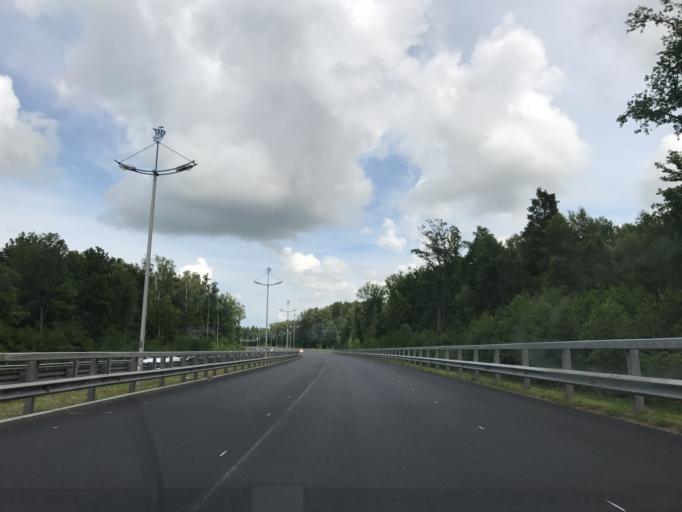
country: RU
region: Kaliningrad
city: Gur'yevsk
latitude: 54.8257
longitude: 20.5770
